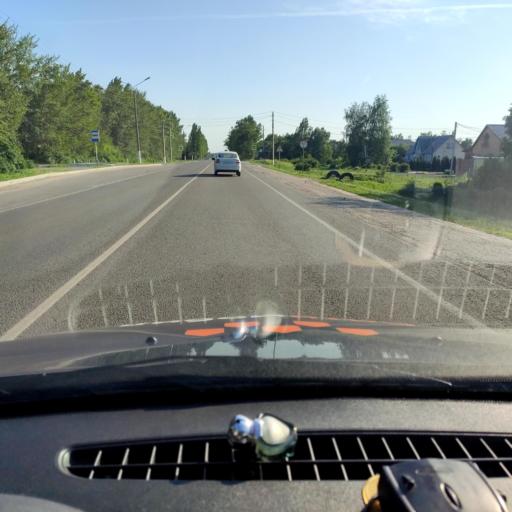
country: RU
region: Voronezj
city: Novaya Usman'
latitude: 51.6528
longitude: 39.4274
